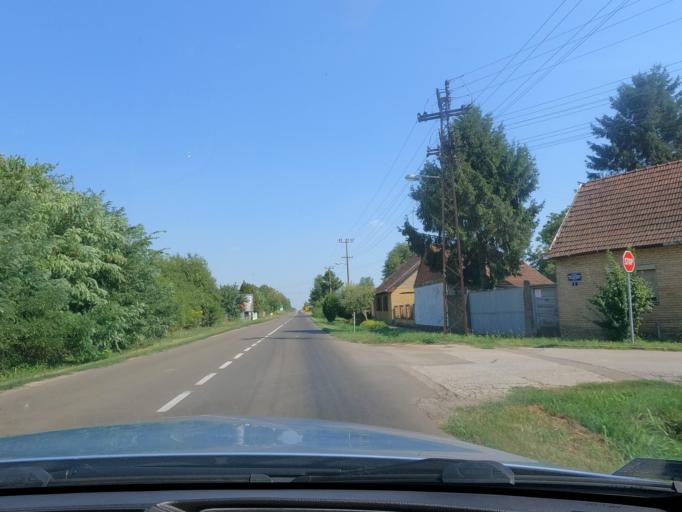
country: RS
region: Autonomna Pokrajina Vojvodina
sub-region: Severnobacki Okrug
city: Backa Topola
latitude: 45.8034
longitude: 19.6511
